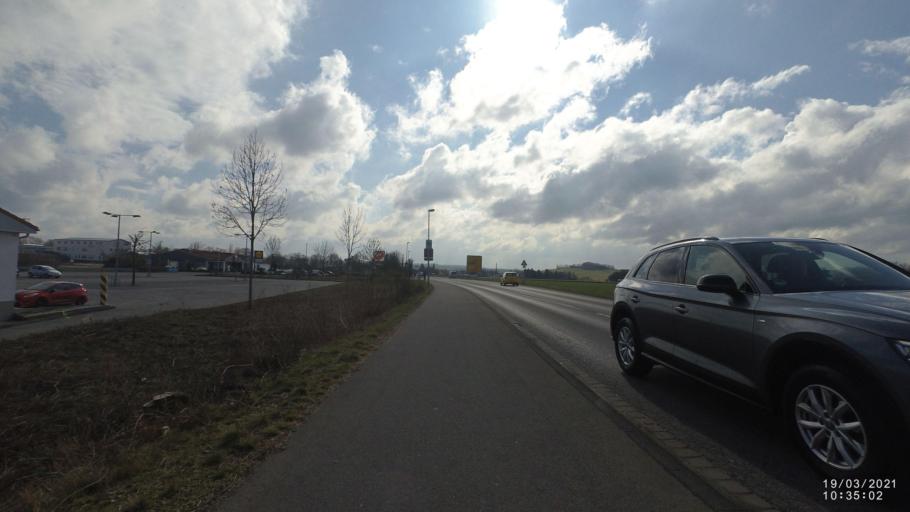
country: DE
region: Rheinland-Pfalz
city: Mendig
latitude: 50.3664
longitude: 7.2932
